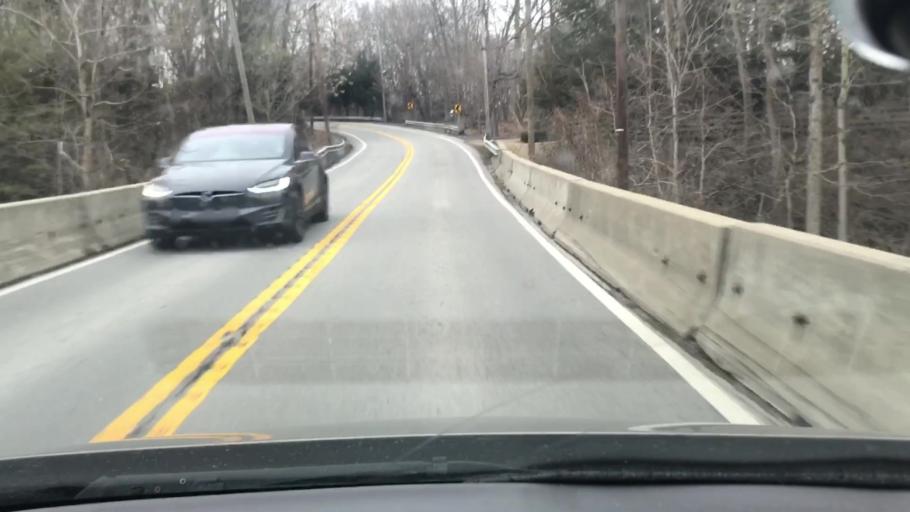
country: US
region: Kentucky
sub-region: Jefferson County
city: Barbourmeade
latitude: 38.2925
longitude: -85.6109
